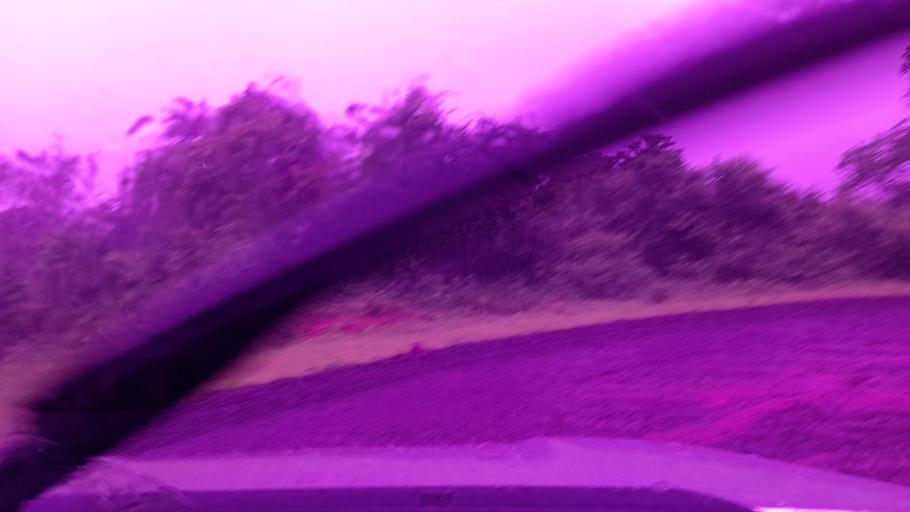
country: ET
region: Oromiya
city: Metu
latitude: 8.4725
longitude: 35.6384
